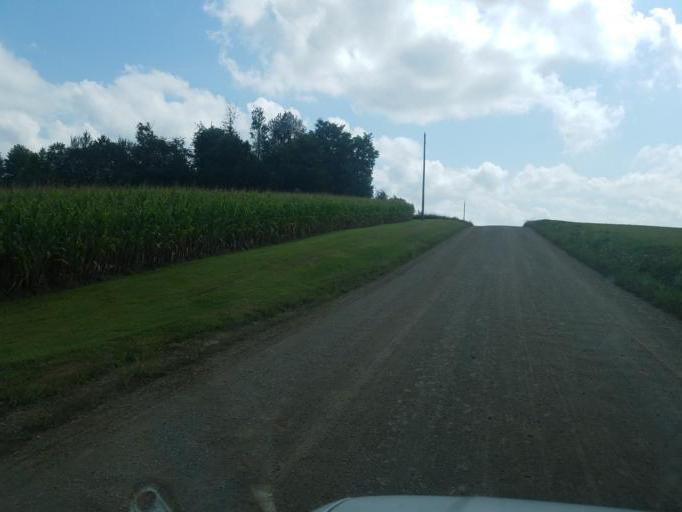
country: US
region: Ohio
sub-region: Knox County
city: Danville
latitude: 40.5469
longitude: -82.3598
